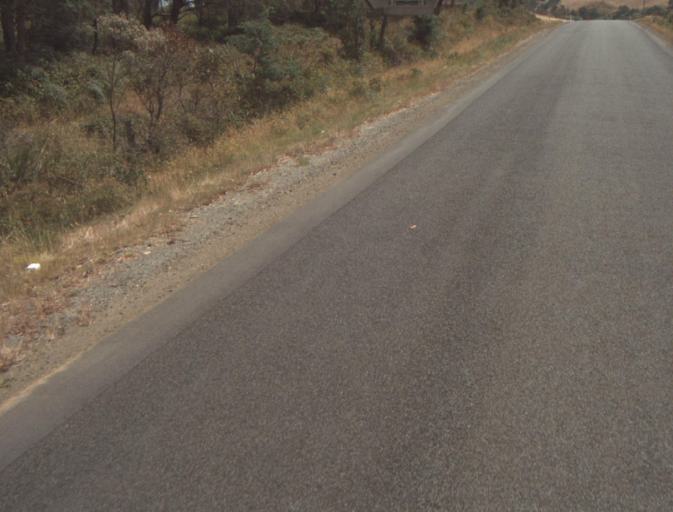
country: AU
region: Tasmania
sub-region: Launceston
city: Mayfield
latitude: -41.2300
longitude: 147.1450
